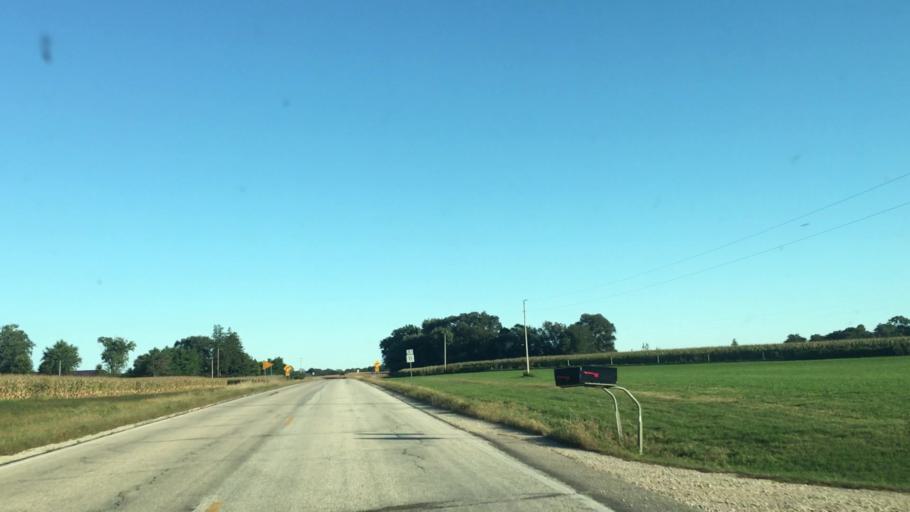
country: US
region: Minnesota
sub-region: Fillmore County
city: Chatfield
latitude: 43.8375
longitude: -92.0732
